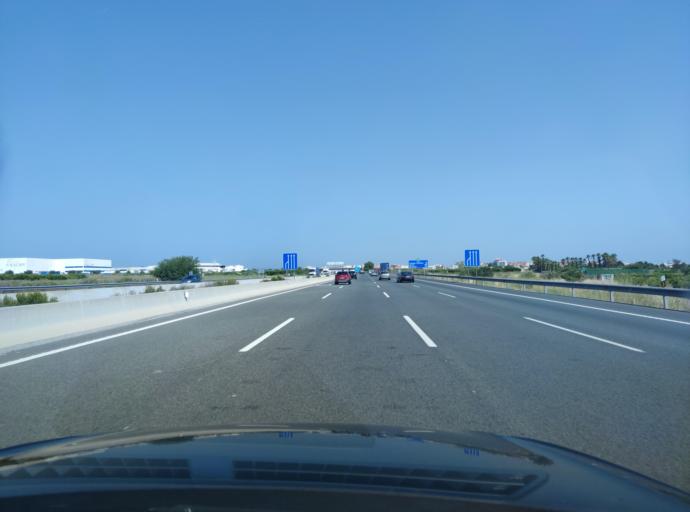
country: ES
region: Valencia
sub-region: Provincia de Valencia
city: Alcasser
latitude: 39.3553
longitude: -0.4368
